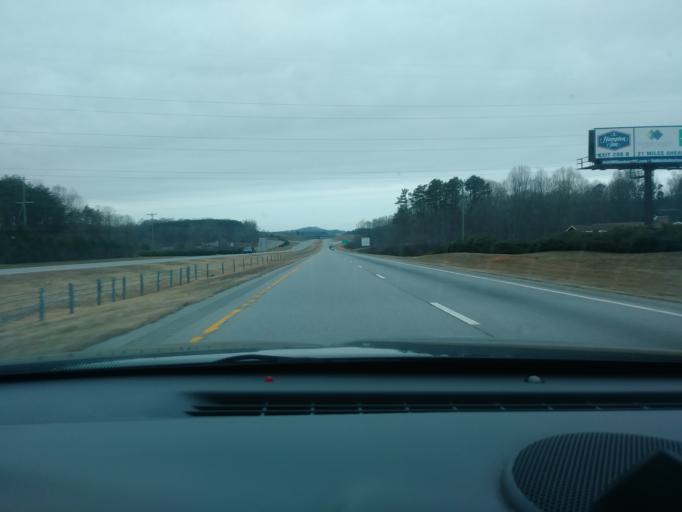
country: US
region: North Carolina
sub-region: Yadkin County
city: Jonesville
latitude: 36.1272
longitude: -80.8312
